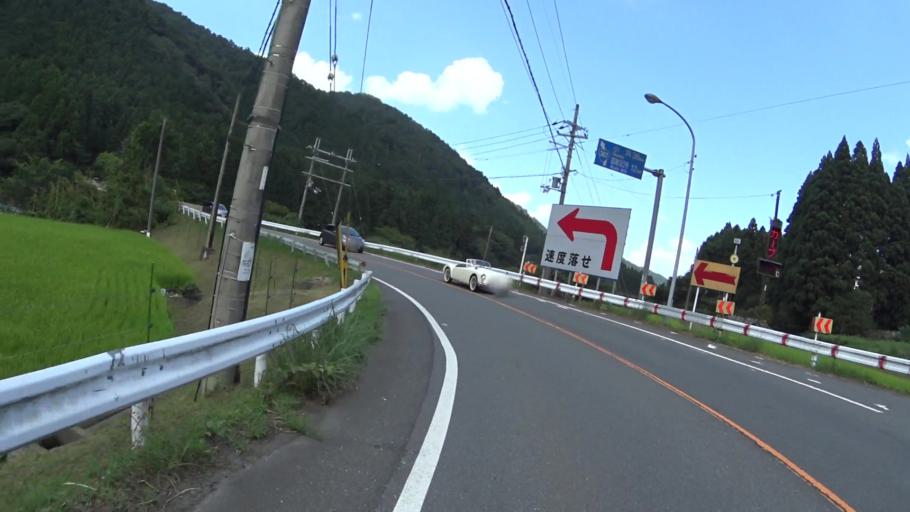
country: JP
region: Shiga Prefecture
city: Kitahama
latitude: 35.3265
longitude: 135.8997
